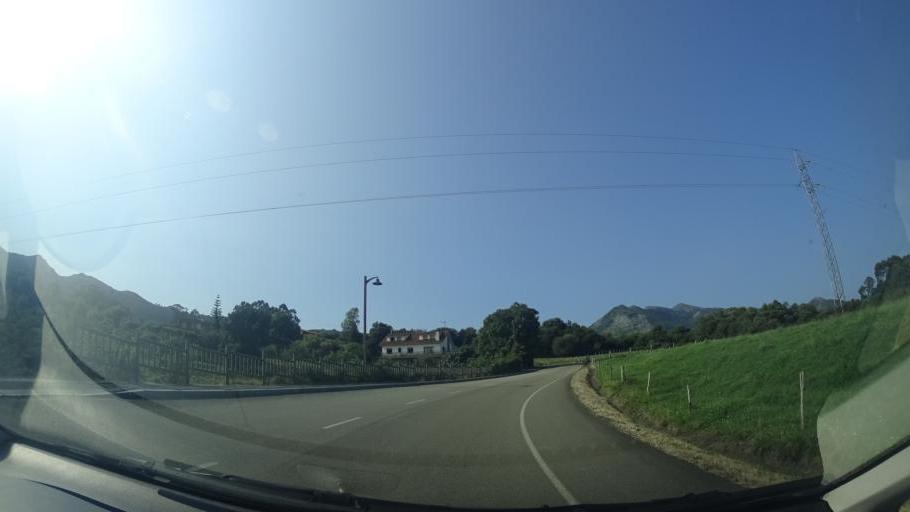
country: ES
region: Asturias
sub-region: Province of Asturias
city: Colunga
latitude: 43.4691
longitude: -5.1891
